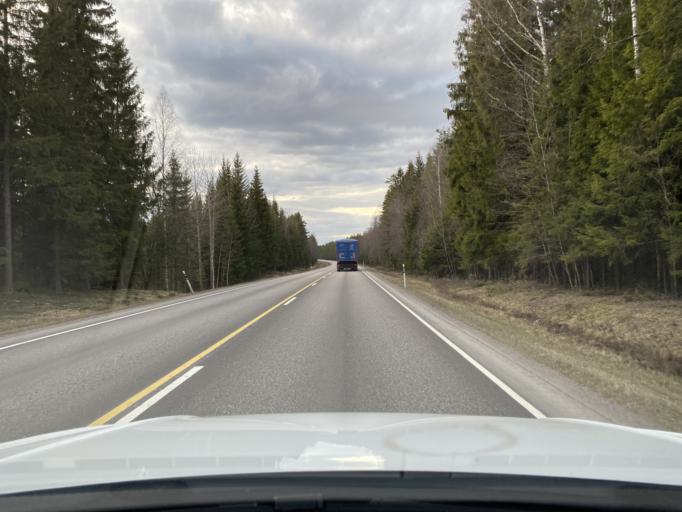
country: FI
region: Uusimaa
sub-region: Helsinki
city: Kaerkoelae
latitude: 60.8066
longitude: 24.0678
